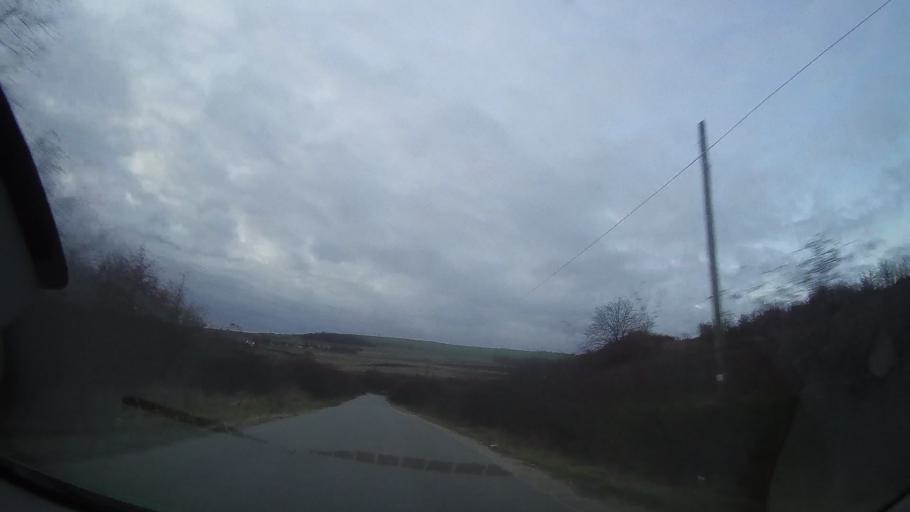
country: RO
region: Cluj
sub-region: Comuna Caianu
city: Vaida-Camaras
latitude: 46.8337
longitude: 23.9638
